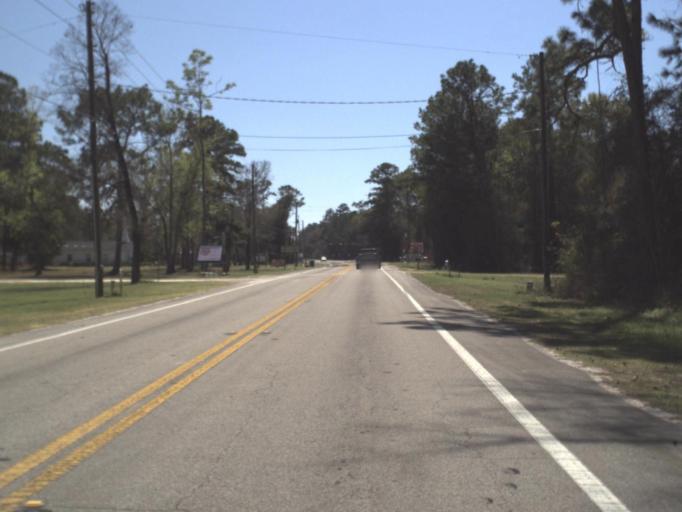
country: US
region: Florida
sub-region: Leon County
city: Woodville
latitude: 30.2360
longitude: -84.2308
